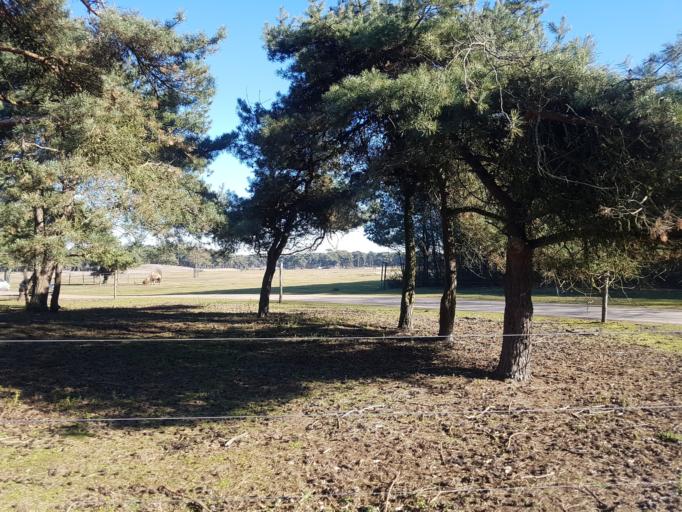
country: NL
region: North Brabant
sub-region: Gemeente Goirle
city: Goirle
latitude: 51.5160
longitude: 5.0979
